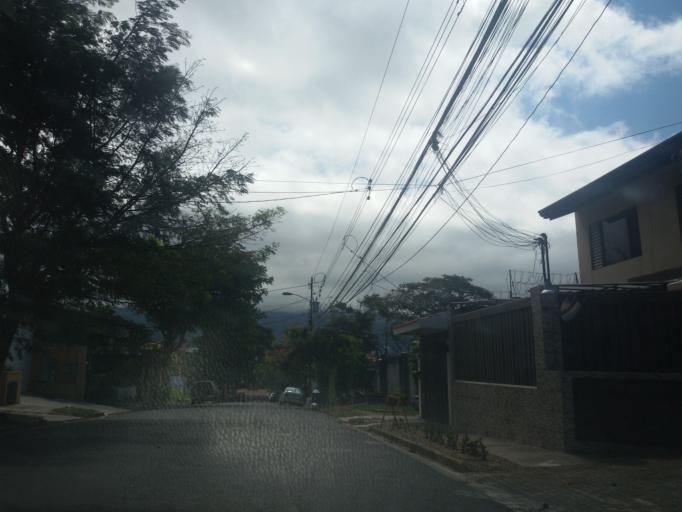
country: CR
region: San Jose
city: San Rafael
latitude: 9.9584
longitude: -84.1222
